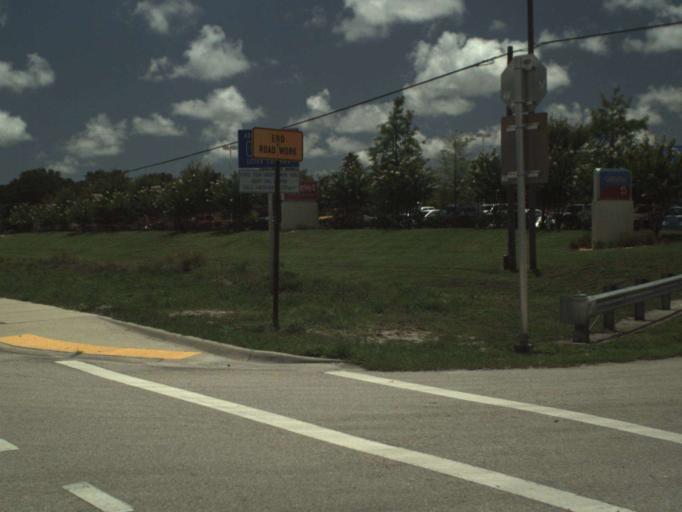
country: US
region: Florida
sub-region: Indian River County
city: West Vero Corridor
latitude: 27.6391
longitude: -80.5116
